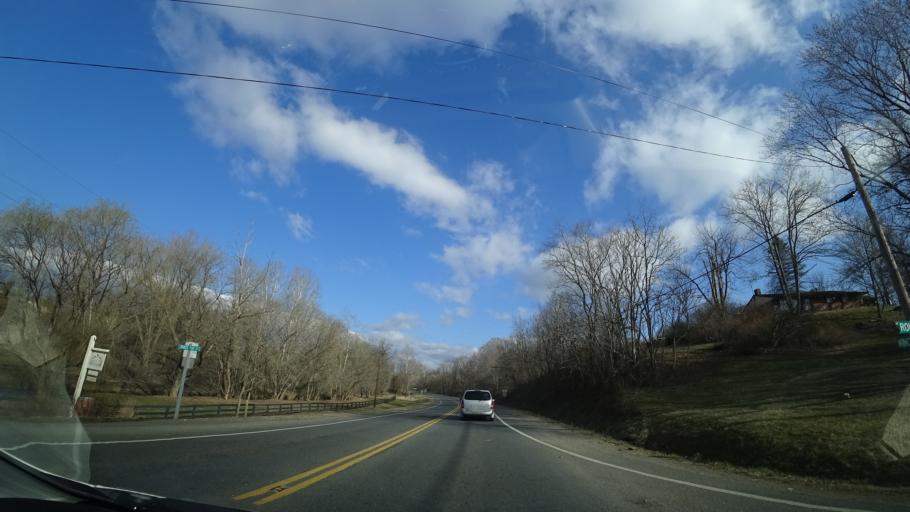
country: US
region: Virginia
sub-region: Fauquier County
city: Marshall
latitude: 38.9150
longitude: -77.9220
